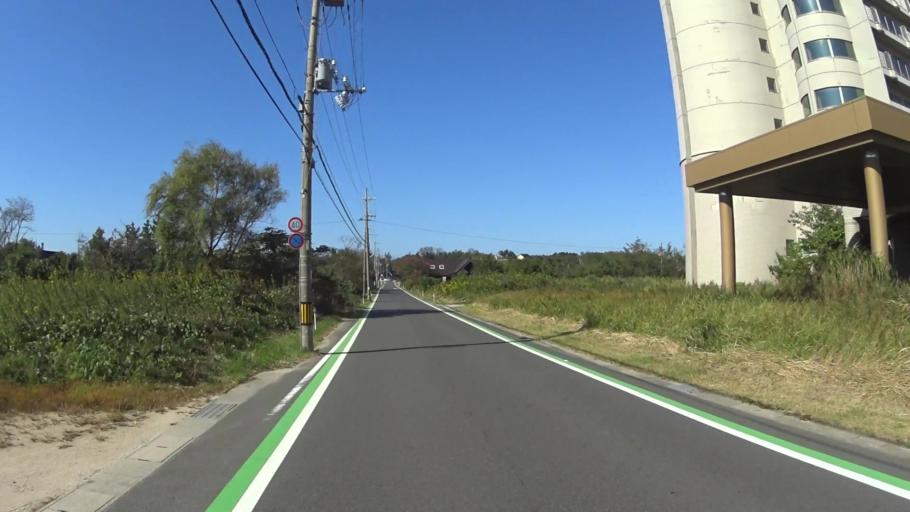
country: JP
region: Hyogo
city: Toyooka
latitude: 35.6351
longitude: 134.9289
